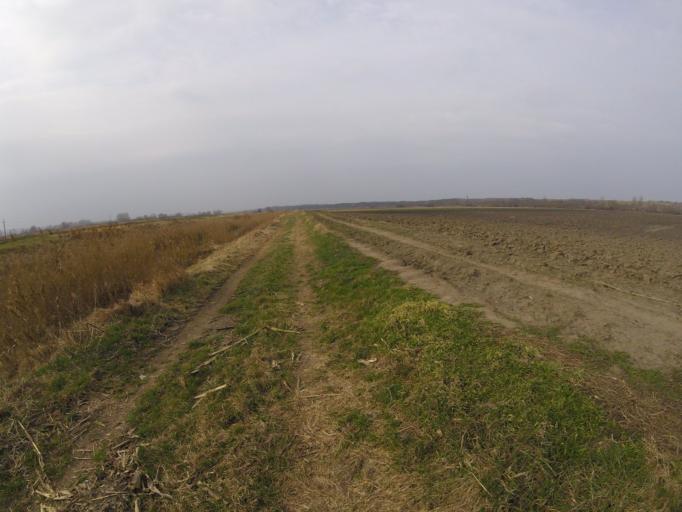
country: HU
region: Pest
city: Galgaheviz
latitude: 47.6284
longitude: 19.5517
